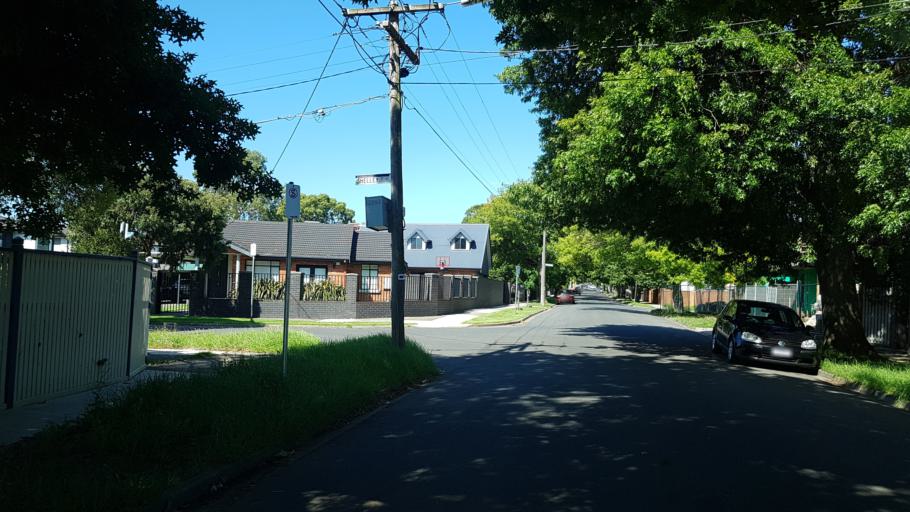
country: AU
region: Victoria
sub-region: Banyule
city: Heidelberg Heights
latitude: -37.7438
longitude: 145.0505
